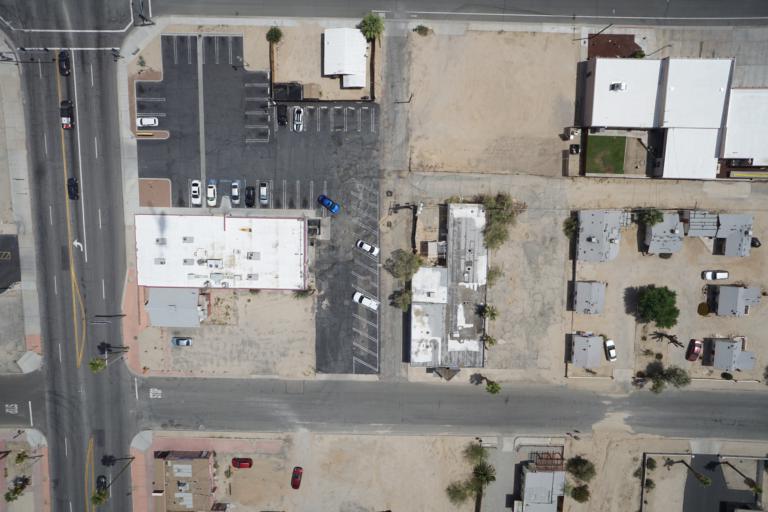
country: US
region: California
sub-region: San Bernardino County
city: Twentynine Palms
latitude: 34.1350
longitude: -116.0549
